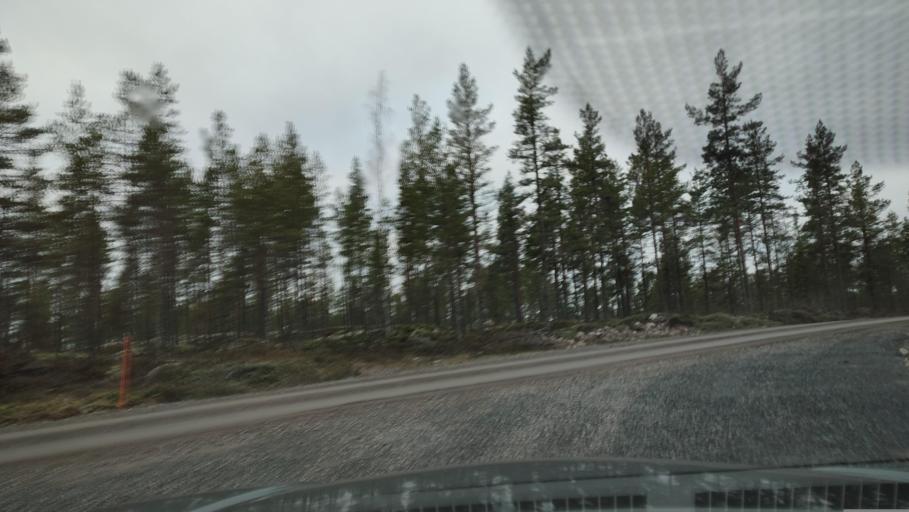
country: FI
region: Southern Ostrobothnia
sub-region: Suupohja
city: Karijoki
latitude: 62.1994
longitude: 21.5900
